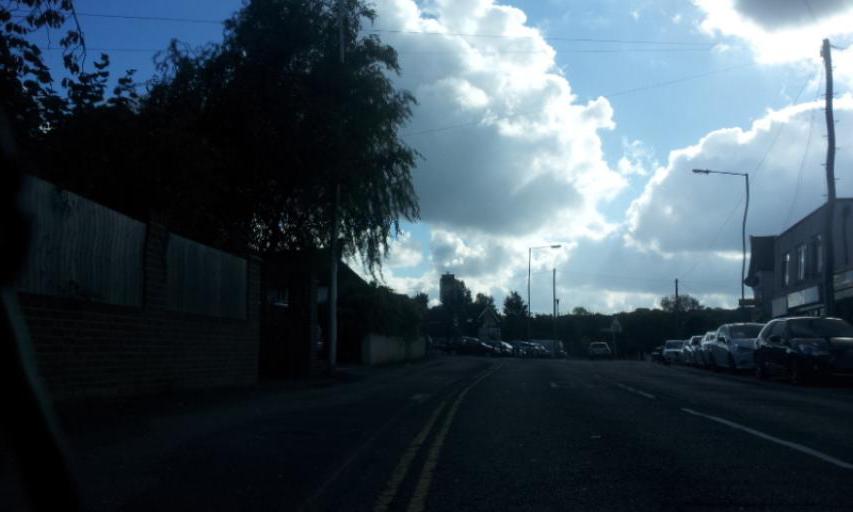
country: GB
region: England
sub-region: Kent
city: Rainham
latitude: 51.3535
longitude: 0.5803
